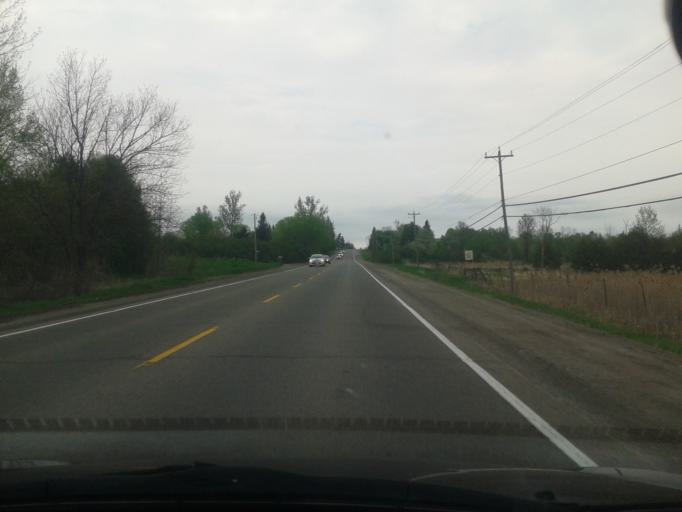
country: CA
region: Ontario
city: Kingston
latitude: 44.4233
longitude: -76.6674
